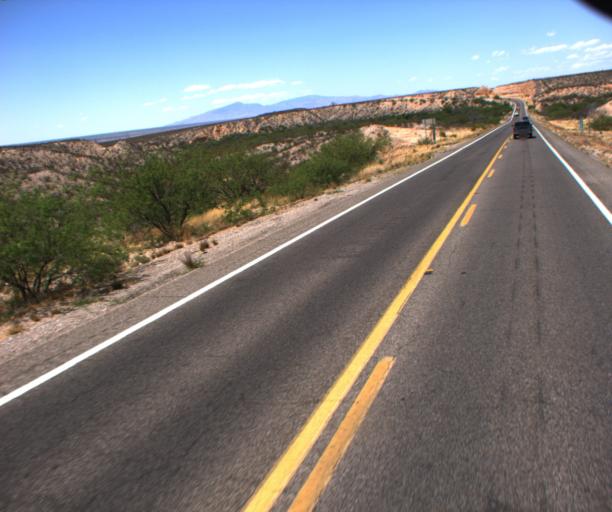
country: US
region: Arizona
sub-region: Cochise County
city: Saint David
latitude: 31.8107
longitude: -110.1642
